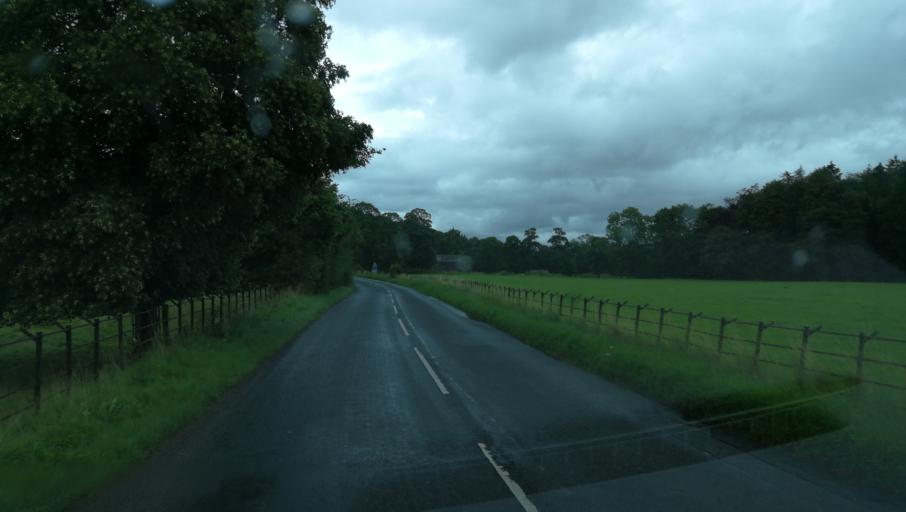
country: GB
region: England
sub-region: Cumbria
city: Penrith
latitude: 54.6347
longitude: -2.8077
